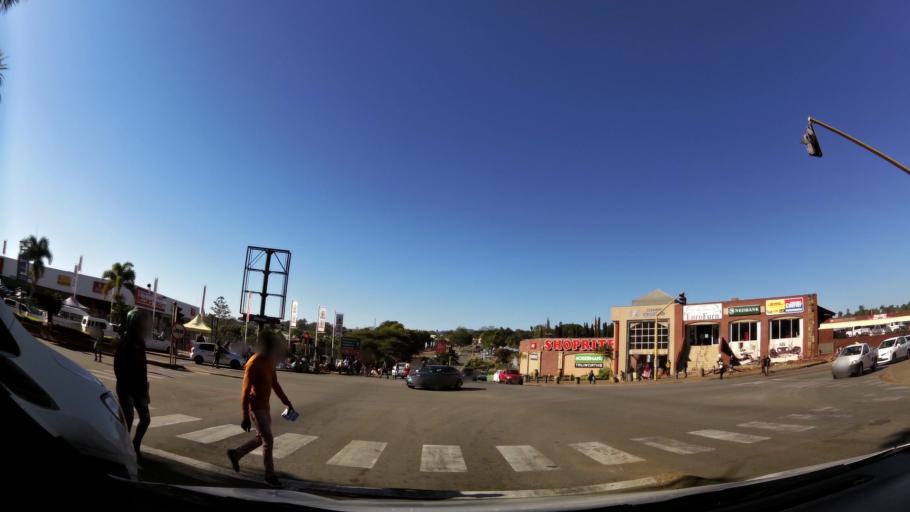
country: ZA
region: Limpopo
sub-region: Mopani District Municipality
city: Tzaneen
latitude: -23.8286
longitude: 30.1618
